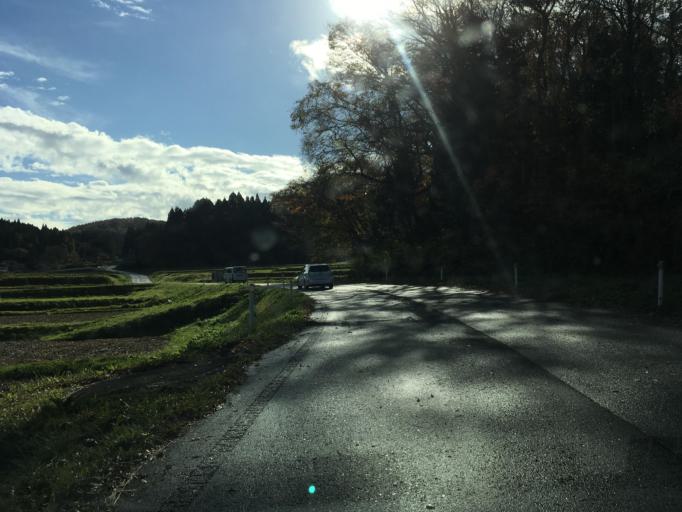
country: JP
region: Iwate
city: Ichinoseki
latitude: 38.8920
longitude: 141.4514
